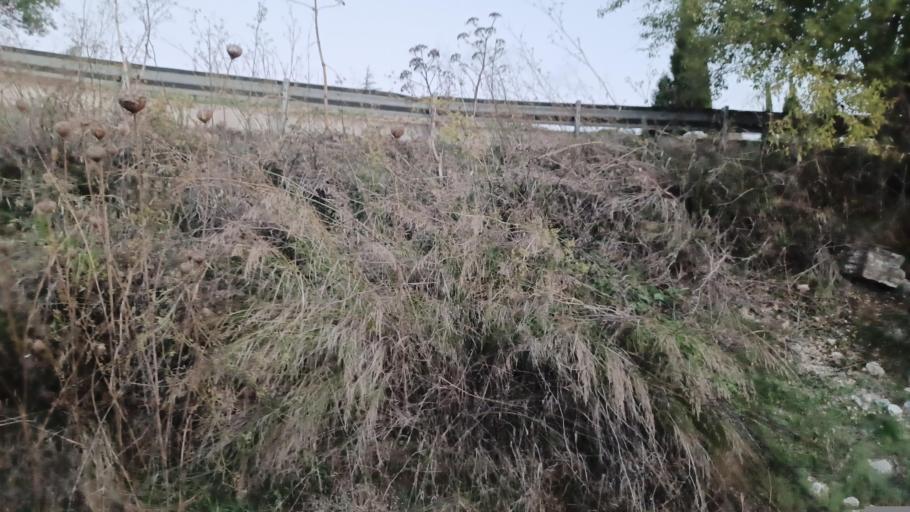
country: CY
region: Pafos
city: Mesogi
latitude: 34.8576
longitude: 32.5034
